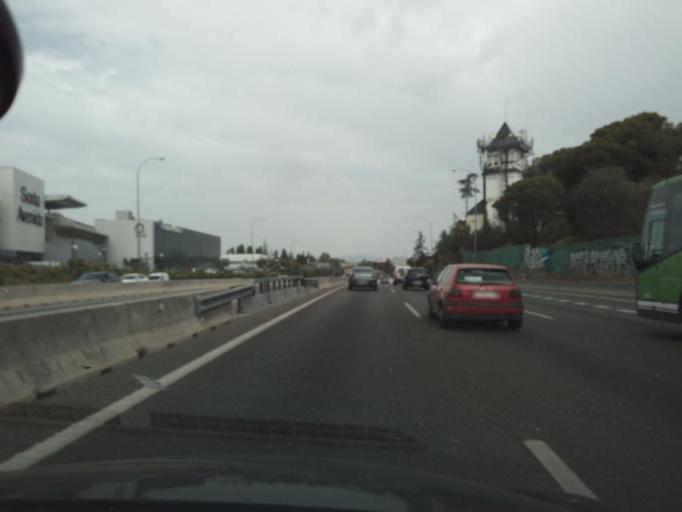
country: ES
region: Madrid
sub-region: Provincia de Madrid
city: Pozuelo de Alarcon
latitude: 40.4681
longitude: -3.8139
